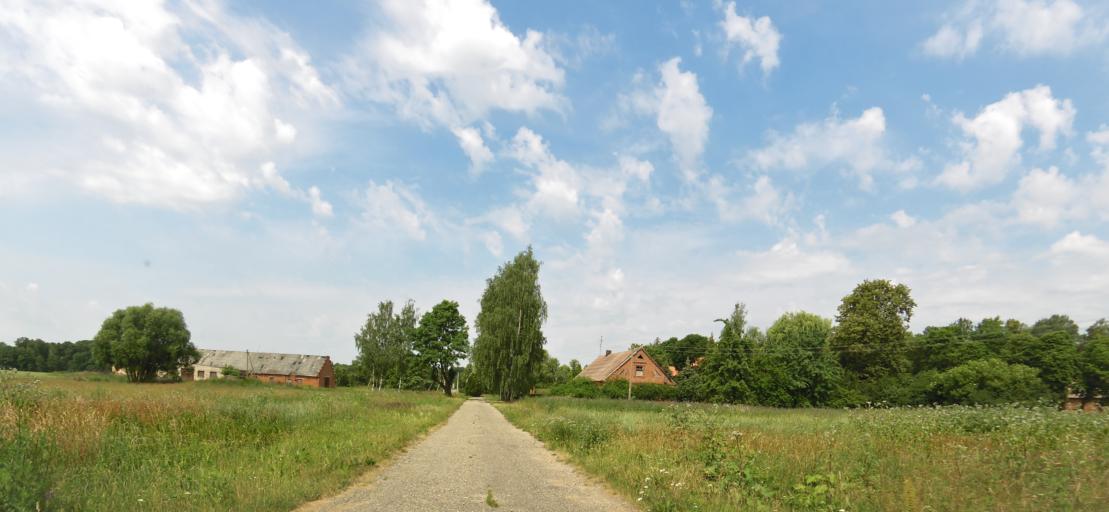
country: LT
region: Panevezys
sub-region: Birzai
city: Birzai
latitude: 56.2875
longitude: 24.6060
